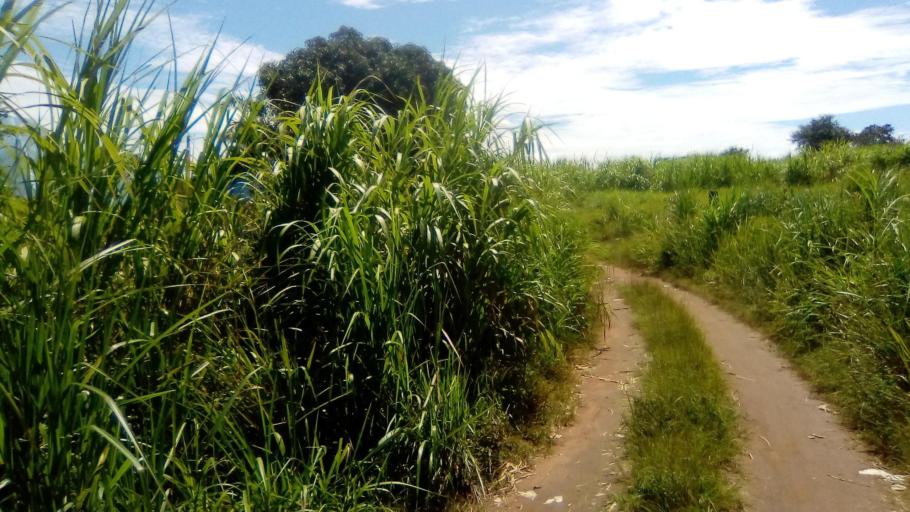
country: SL
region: Eastern Province
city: Simbakoro
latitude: 8.6303
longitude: -10.9999
